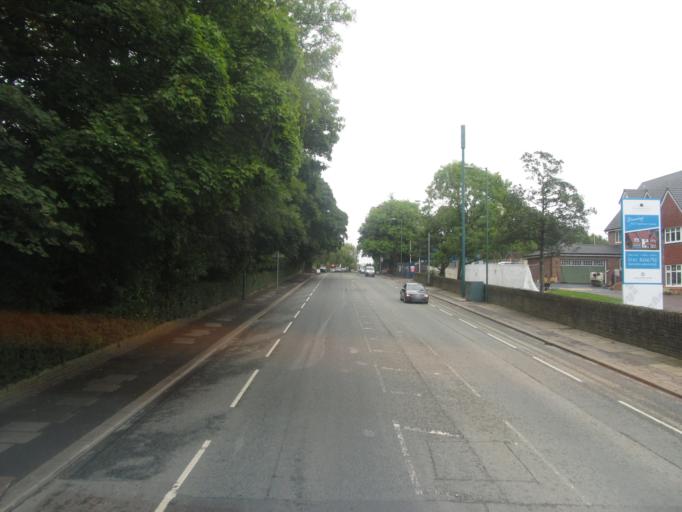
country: GB
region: England
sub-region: Borough of Tameside
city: Haughton Green
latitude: 53.4344
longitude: -2.0831
